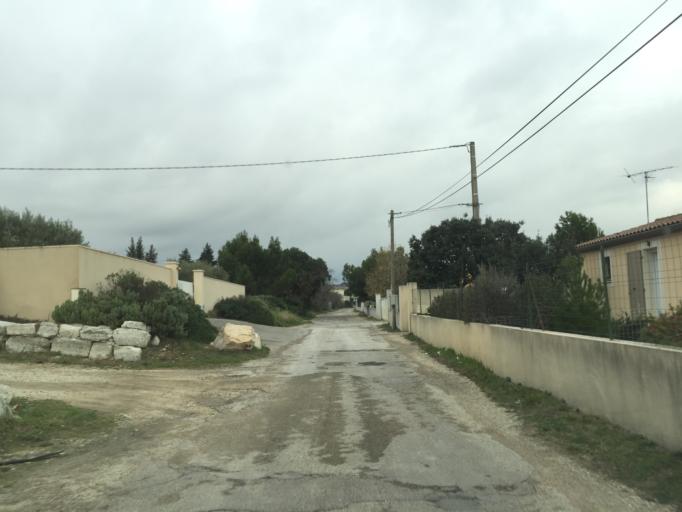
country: FR
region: Provence-Alpes-Cote d'Azur
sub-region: Departement du Vaucluse
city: Sorgues
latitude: 44.0256
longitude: 4.8744
